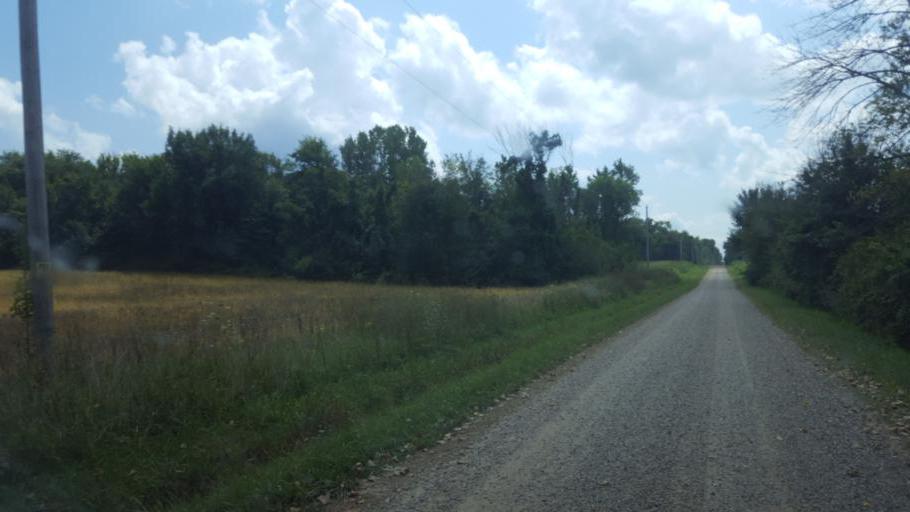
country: US
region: Ohio
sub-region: Knox County
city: Centerburg
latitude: 40.3782
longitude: -82.6330
